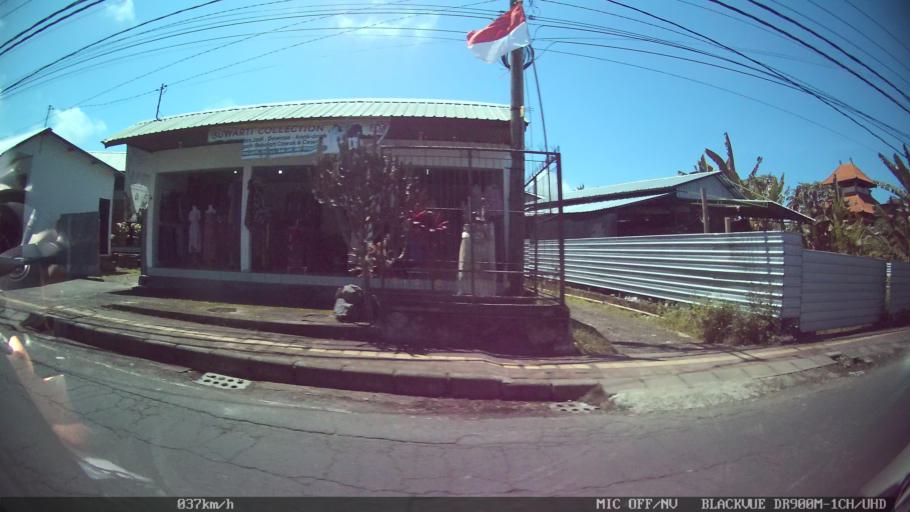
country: ID
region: Bali
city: Klungkung
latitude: -8.5631
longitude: 115.3400
